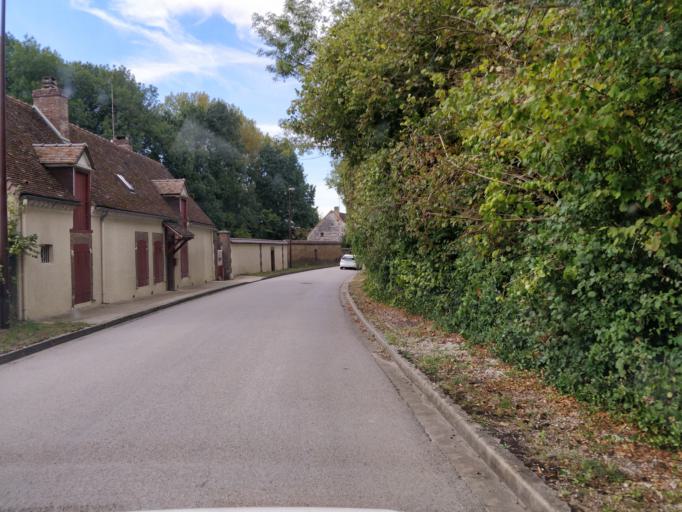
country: FR
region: Champagne-Ardenne
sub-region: Departement de l'Aube
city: Aix-en-Othe
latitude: 48.2055
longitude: 3.6347
